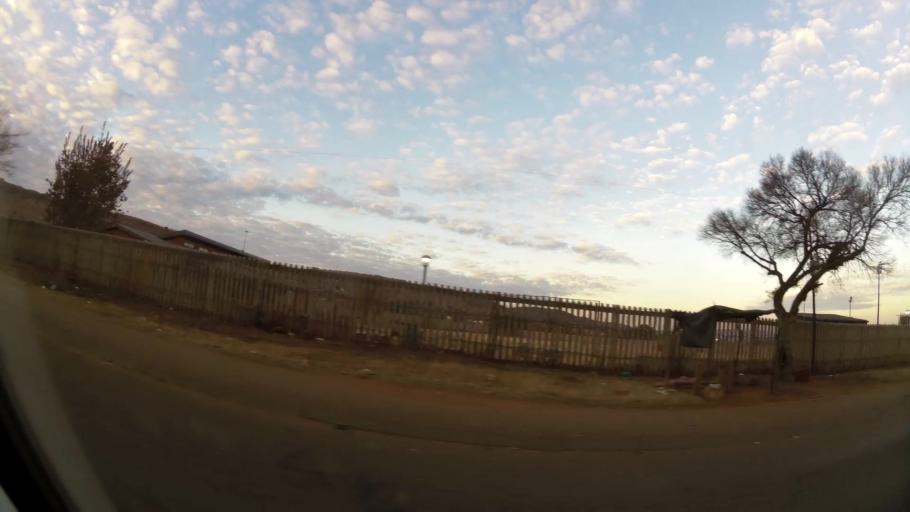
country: ZA
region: Gauteng
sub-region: City of Tshwane Metropolitan Municipality
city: Pretoria
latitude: -25.7059
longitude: 28.3363
